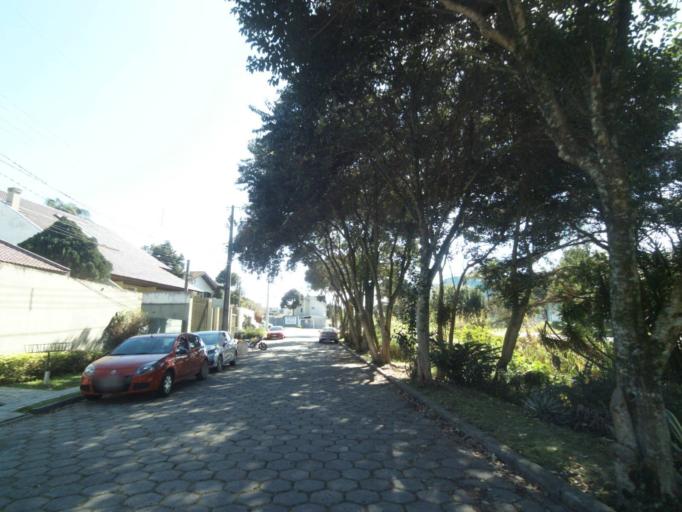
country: BR
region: Parana
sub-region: Curitiba
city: Curitiba
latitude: -25.4116
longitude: -49.2366
